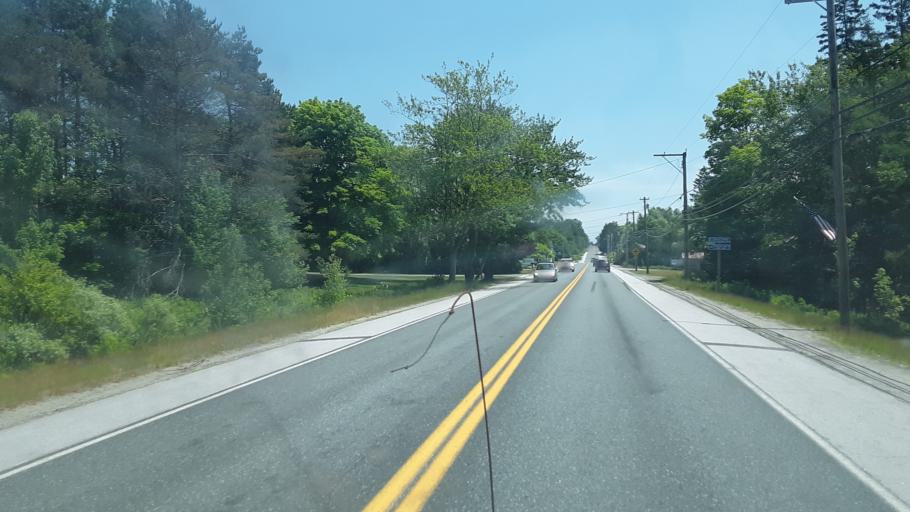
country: US
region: Maine
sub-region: Hancock County
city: Hancock
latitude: 44.5300
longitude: -68.2579
